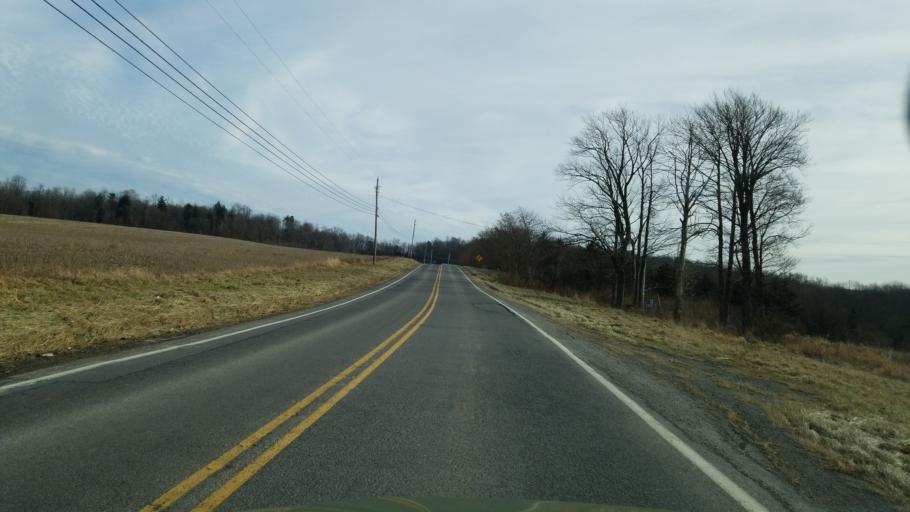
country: US
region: Pennsylvania
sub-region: Indiana County
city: Johnsonburg
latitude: 40.9202
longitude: -78.8549
